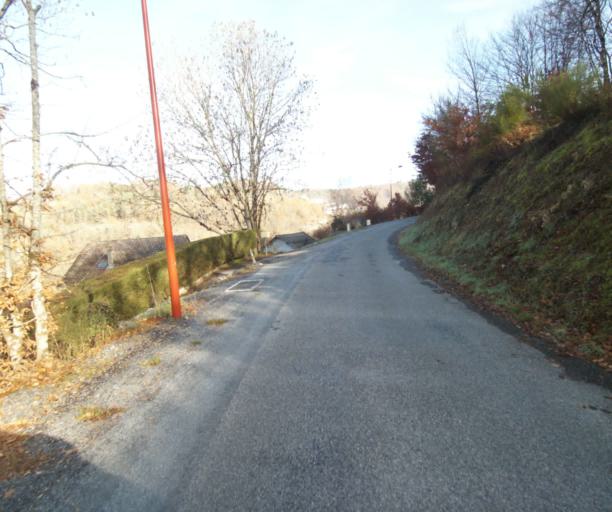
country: FR
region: Limousin
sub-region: Departement de la Correze
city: Laguenne
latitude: 45.2447
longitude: 1.7795
